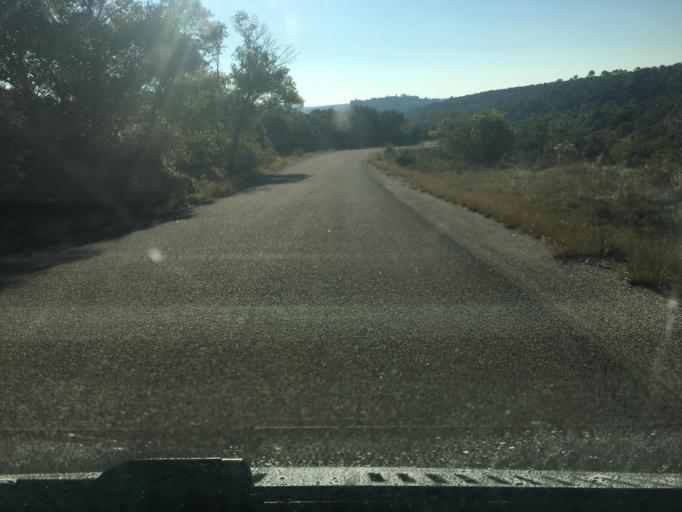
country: FR
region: Languedoc-Roussillon
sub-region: Departement du Gard
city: Goudargues
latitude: 44.1672
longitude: 4.3500
